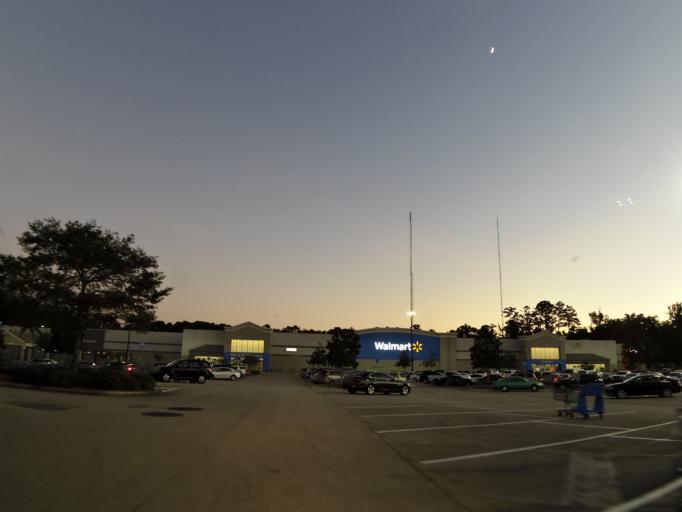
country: US
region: Florida
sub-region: Duval County
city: Jacksonville
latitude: 30.2851
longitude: -81.5627
